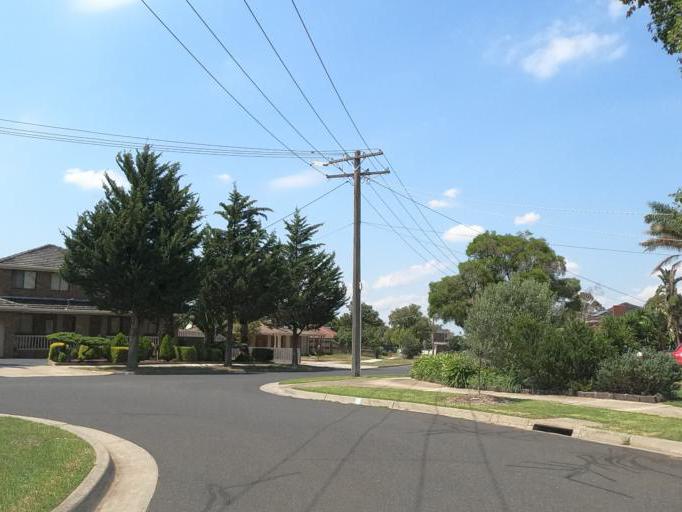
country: AU
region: Victoria
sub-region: Hume
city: Greenvale
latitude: -37.6426
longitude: 144.8827
